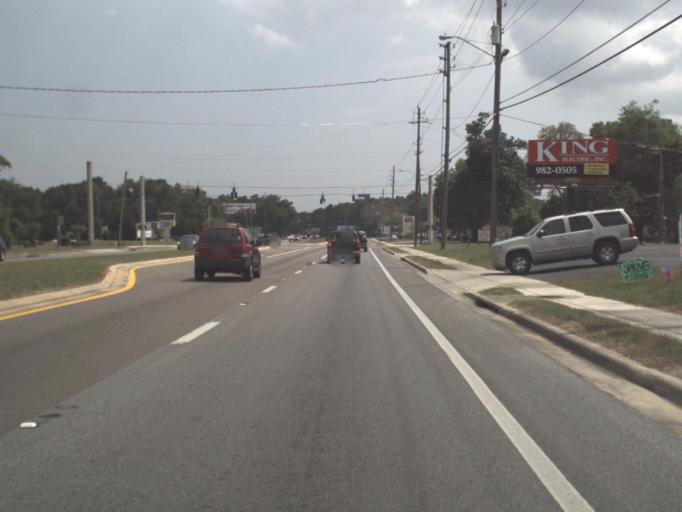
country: US
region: Florida
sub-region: Santa Rosa County
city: Milton
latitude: 30.6243
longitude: -87.0568
